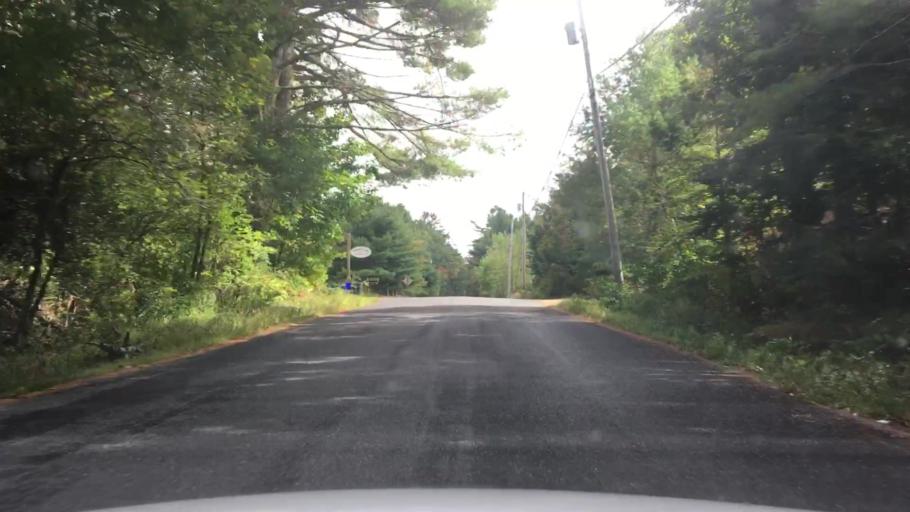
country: US
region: Maine
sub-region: Androscoggin County
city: Lisbon Falls
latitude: 43.9829
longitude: -70.1000
